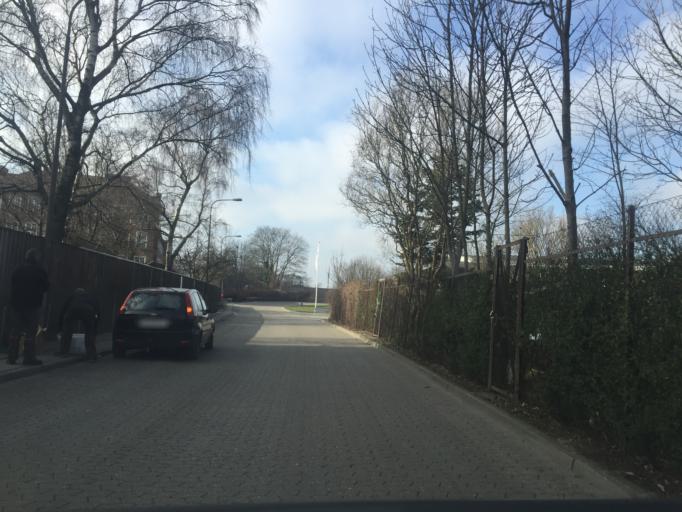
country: DK
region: Capital Region
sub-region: Kobenhavn
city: Copenhagen
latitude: 55.7165
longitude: 12.5708
